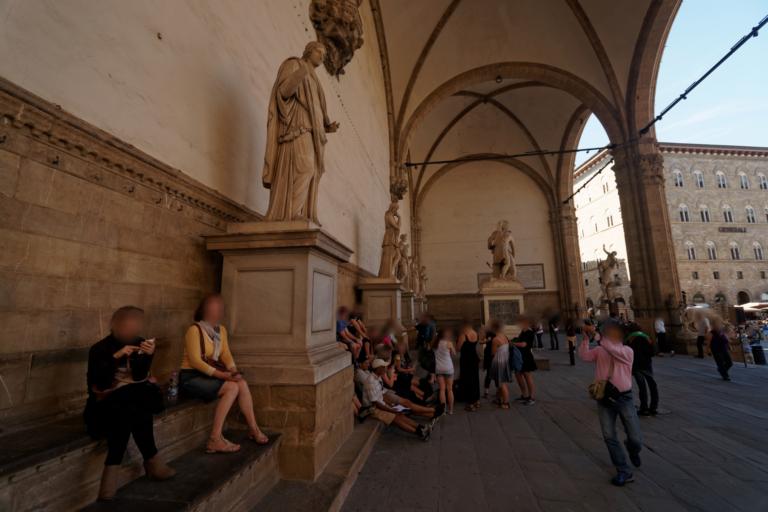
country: IT
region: Tuscany
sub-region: Province of Florence
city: Florence
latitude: 43.7690
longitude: 11.2557
